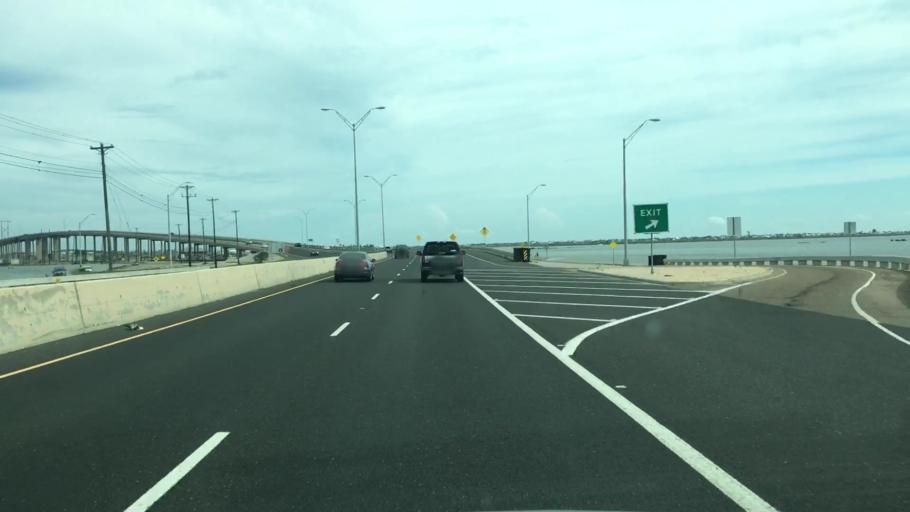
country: US
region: Texas
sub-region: Nueces County
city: Corpus Christi
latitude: 27.6396
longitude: -97.2467
